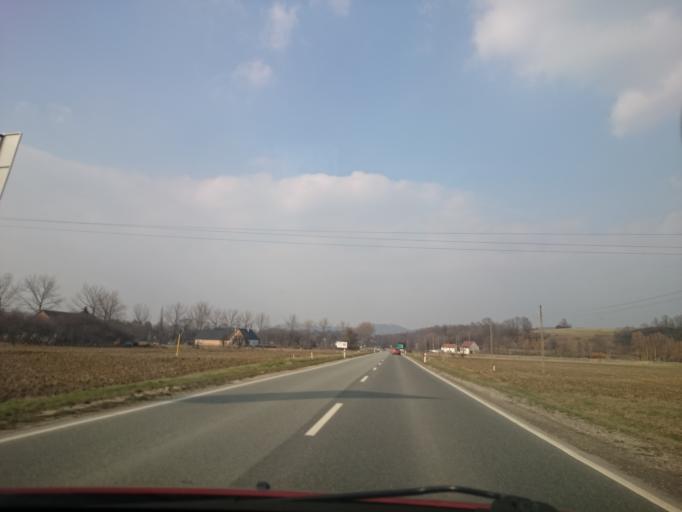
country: PL
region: Lower Silesian Voivodeship
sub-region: Powiat klodzki
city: Bystrzyca Klodzka
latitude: 50.3116
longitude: 16.6605
